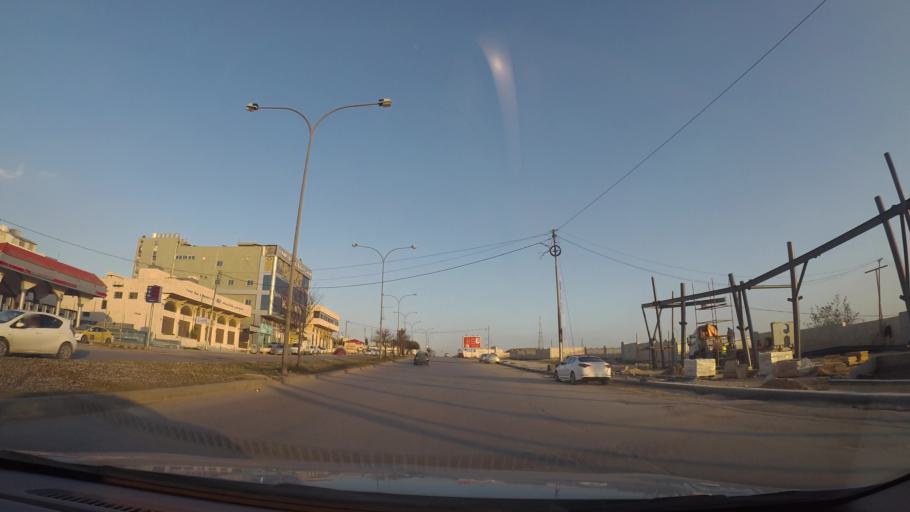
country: JO
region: Amman
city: Al Quwaysimah
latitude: 31.9095
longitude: 35.9267
